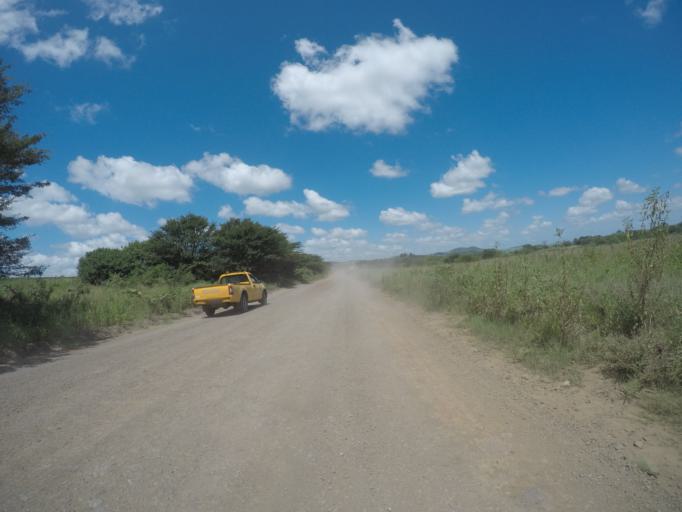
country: ZA
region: KwaZulu-Natal
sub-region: uThungulu District Municipality
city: Empangeni
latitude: -28.6598
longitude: 31.7769
